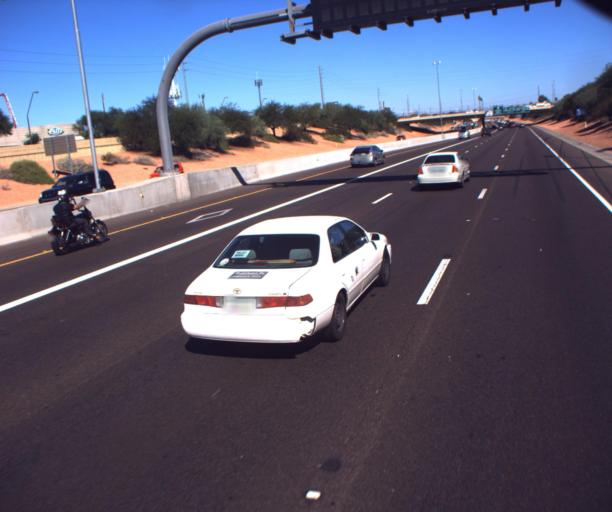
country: US
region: Arizona
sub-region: Maricopa County
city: San Carlos
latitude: 33.3467
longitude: -111.8935
